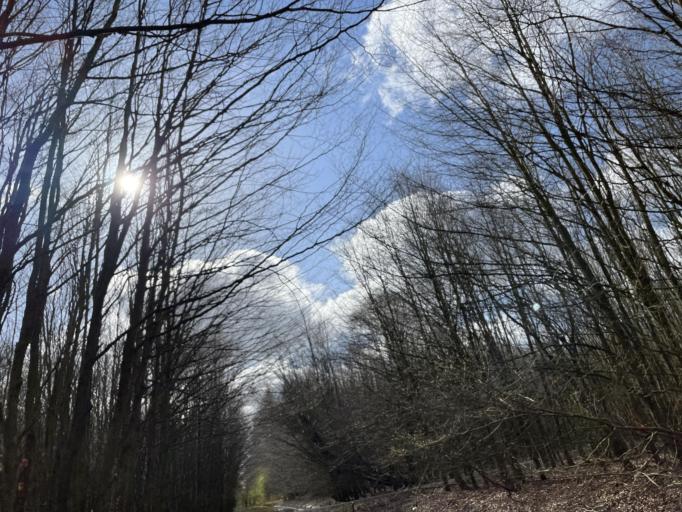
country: NL
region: South Holland
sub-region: Gemeente Pijnacker-Nootdorp
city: Pijnacker
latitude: 52.0457
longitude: 4.4489
